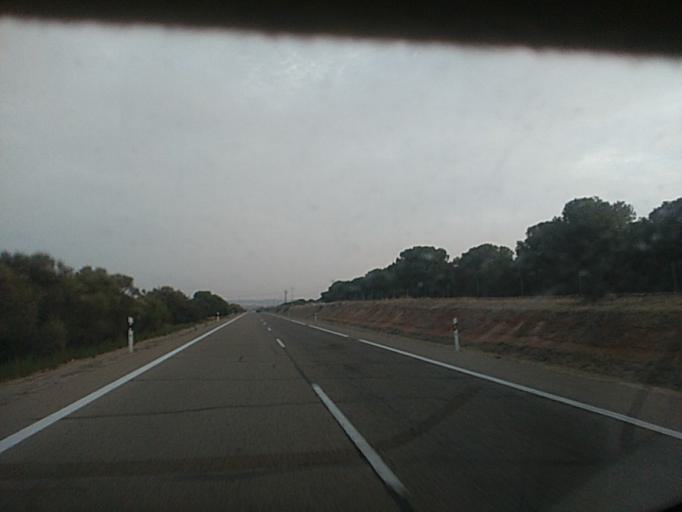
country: ES
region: Castille and Leon
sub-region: Provincia de Valladolid
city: Tordesillas
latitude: 41.4591
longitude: -4.9834
